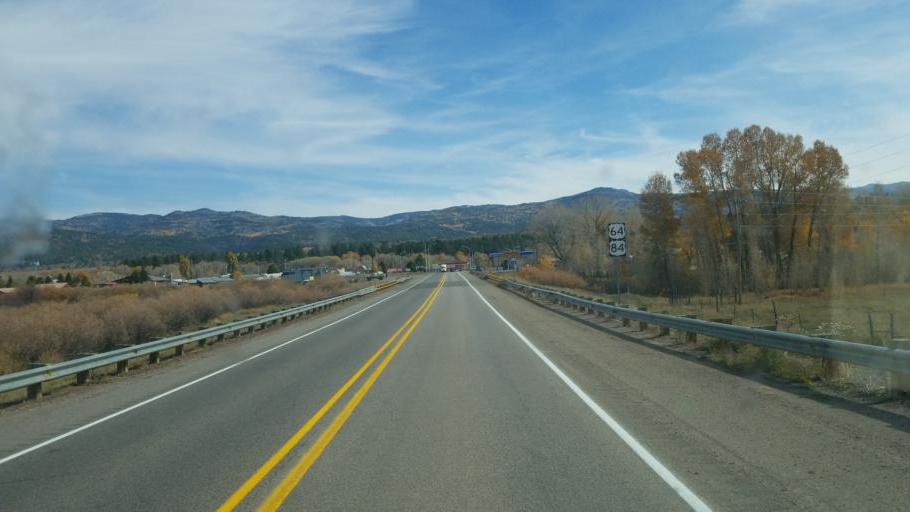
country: US
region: New Mexico
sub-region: Rio Arriba County
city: Chama
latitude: 36.8831
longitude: -106.5894
